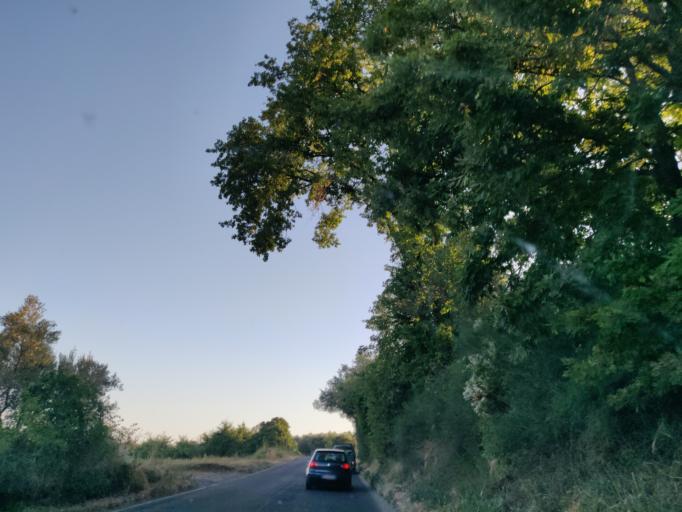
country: IT
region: Latium
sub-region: Provincia di Viterbo
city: Canino
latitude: 42.4531
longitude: 11.7382
